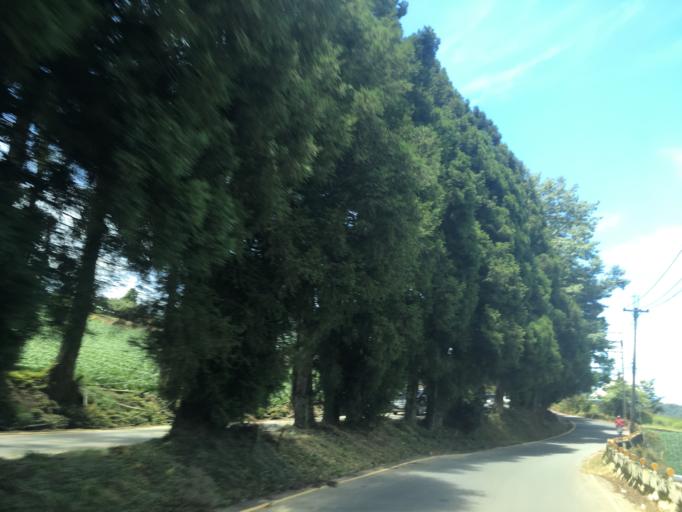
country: TW
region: Taiwan
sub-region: Nantou
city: Puli
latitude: 24.2472
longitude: 121.2430
